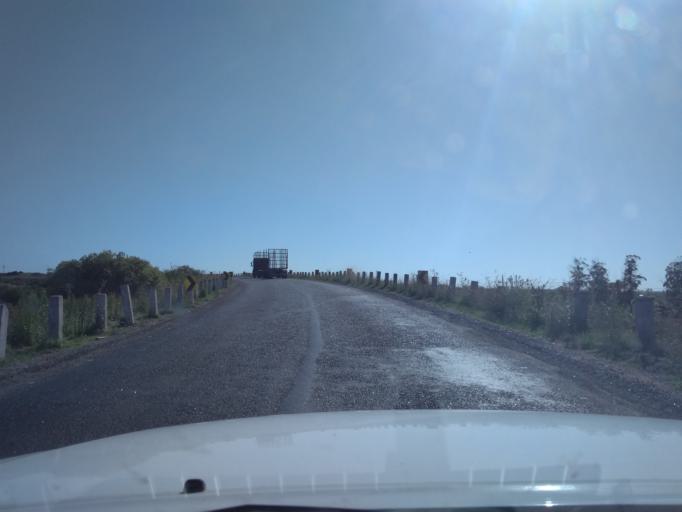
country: UY
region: Canelones
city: San Ramon
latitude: -34.2671
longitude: -55.9305
